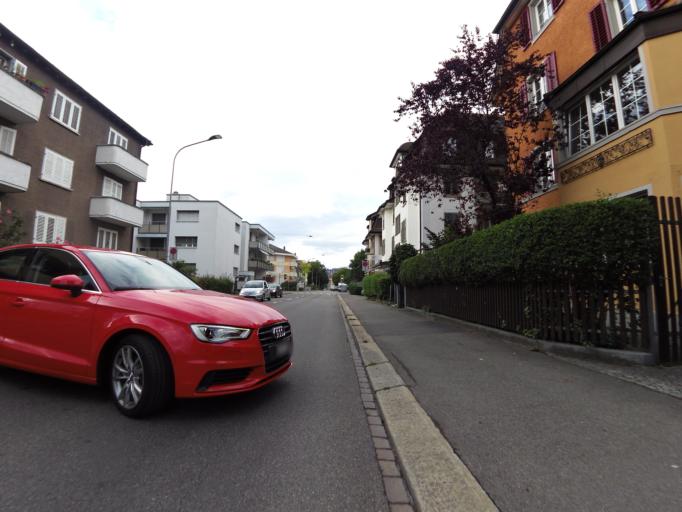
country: CH
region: Zurich
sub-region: Bezirk Zuerich
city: Zuerich (Kreis 9)
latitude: 47.3843
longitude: 8.4846
